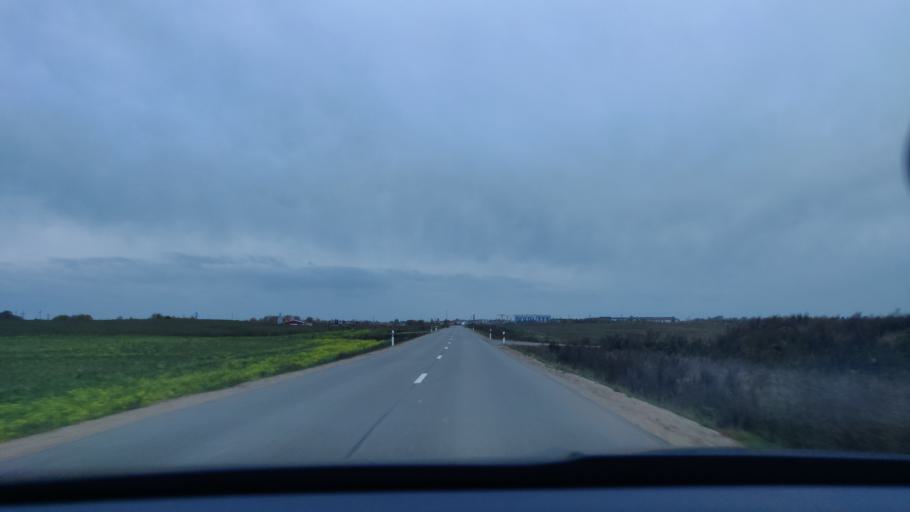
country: LT
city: Lentvaris
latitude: 54.6040
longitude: 25.0029
